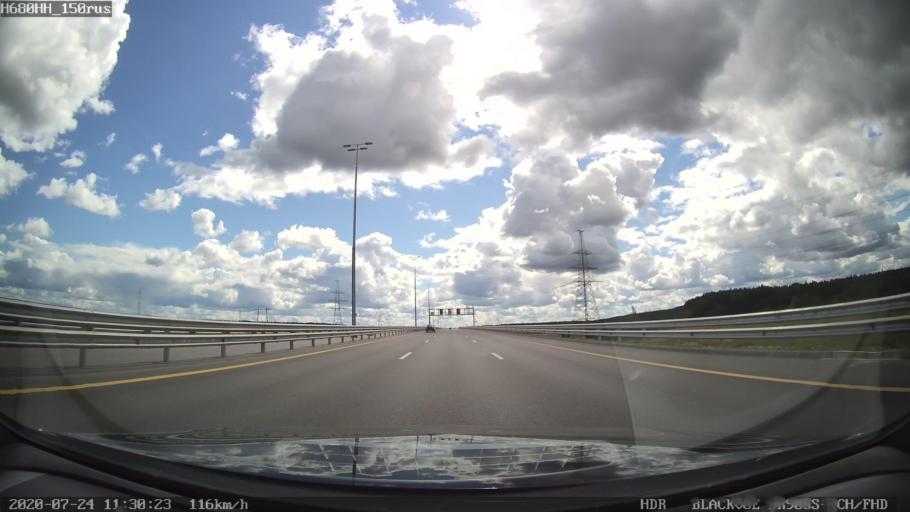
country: RU
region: Leningrad
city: Krasnyy Bor
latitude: 59.6699
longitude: 30.6122
